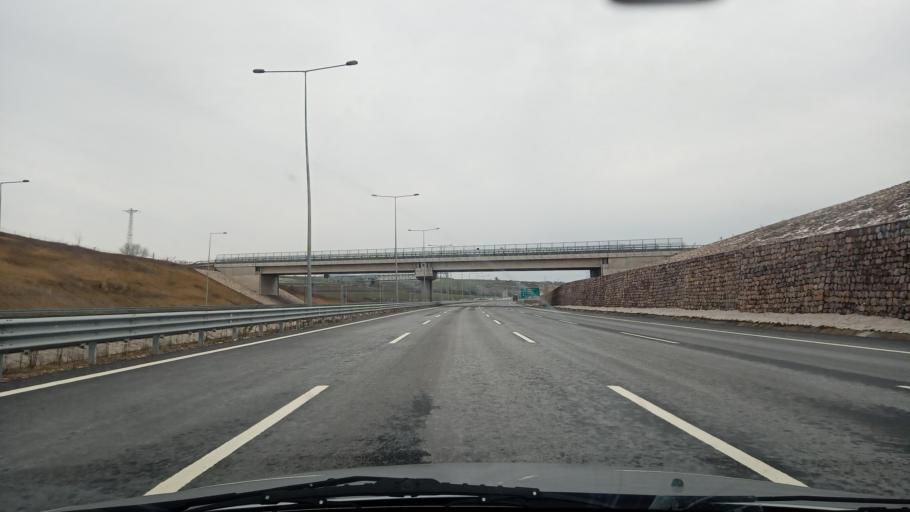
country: TR
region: Kocaeli
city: Kosekoy
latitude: 40.7956
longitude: 30.0553
